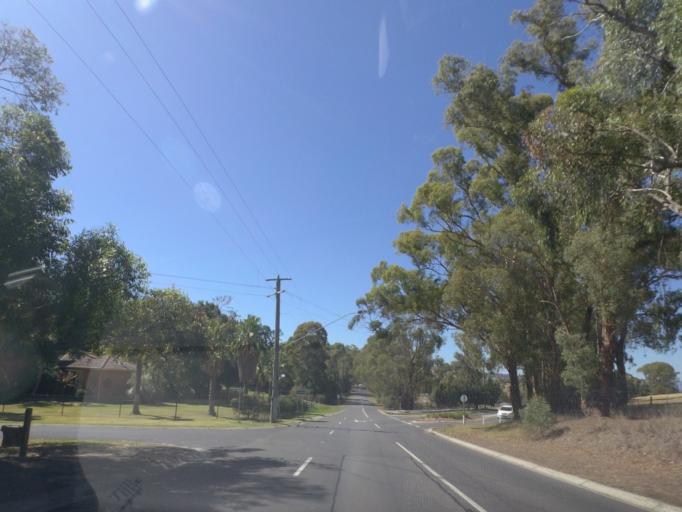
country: AU
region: Victoria
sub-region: Yarra Ranges
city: Chirnside Park
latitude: -37.7331
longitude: 145.2831
